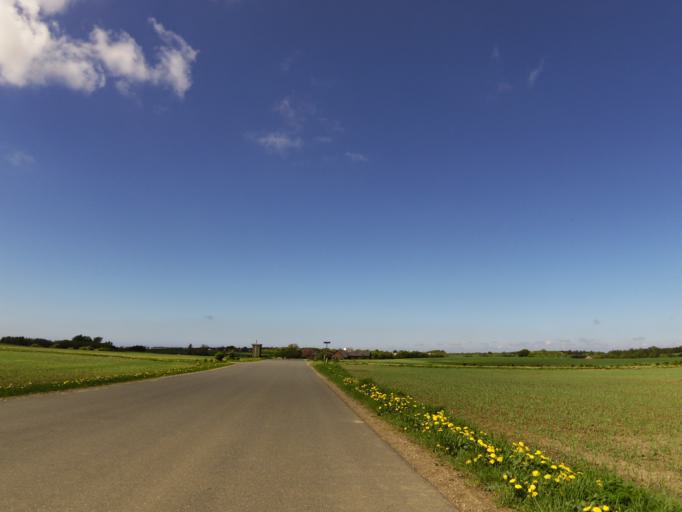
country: DK
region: Central Jutland
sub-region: Holstebro Kommune
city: Vinderup
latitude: 56.4217
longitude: 8.7844
